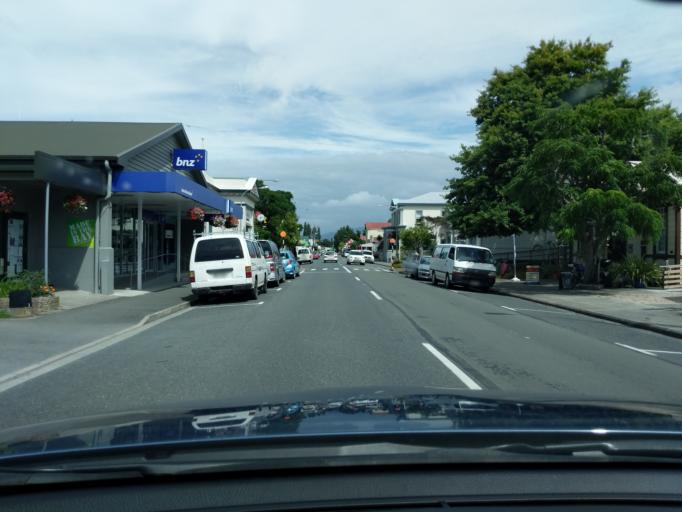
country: NZ
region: Tasman
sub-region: Tasman District
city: Takaka
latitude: -40.8576
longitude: 172.8064
